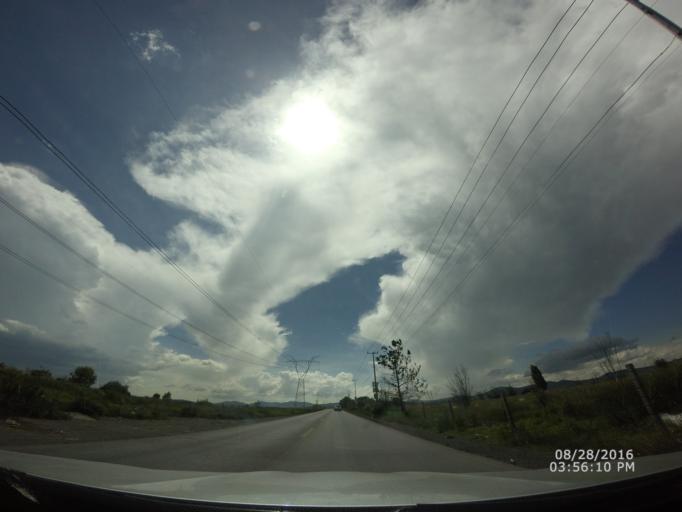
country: MX
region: Hidalgo
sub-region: Mineral de la Reforma
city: Los Tuzos
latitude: 20.0361
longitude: -98.7529
